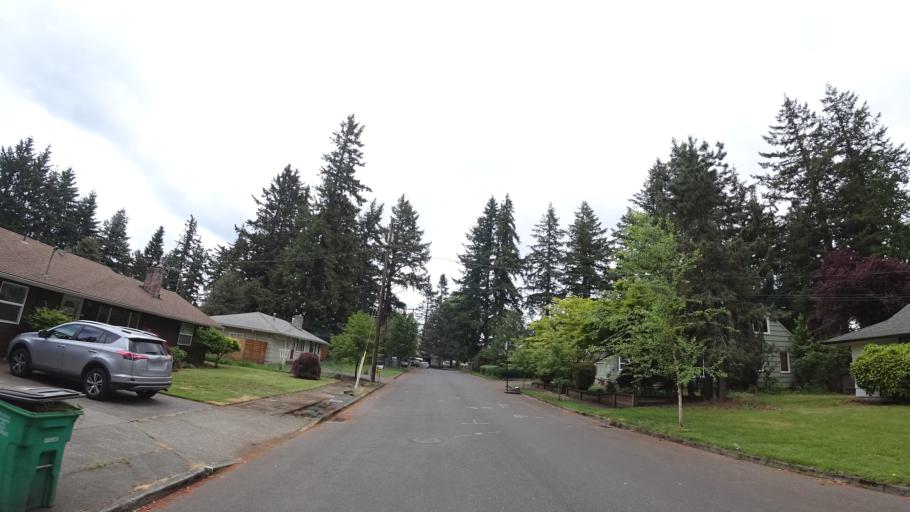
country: US
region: Oregon
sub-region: Multnomah County
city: Lents
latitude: 45.5078
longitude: -122.5330
